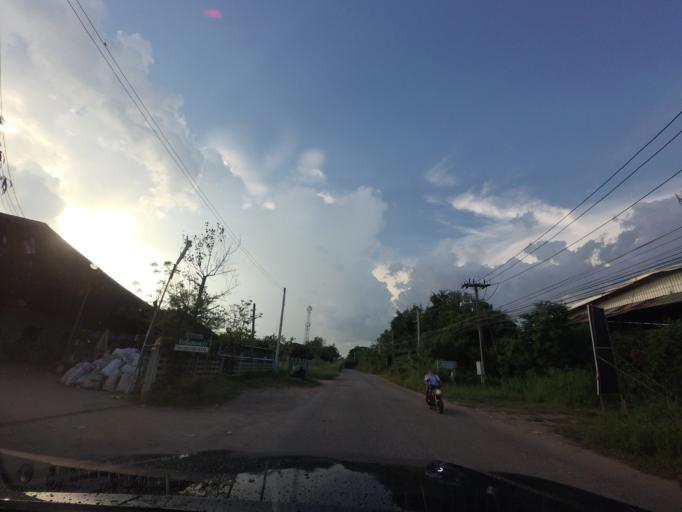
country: TH
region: Khon Kaen
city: Khon Kaen
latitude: 16.4003
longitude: 102.8682
